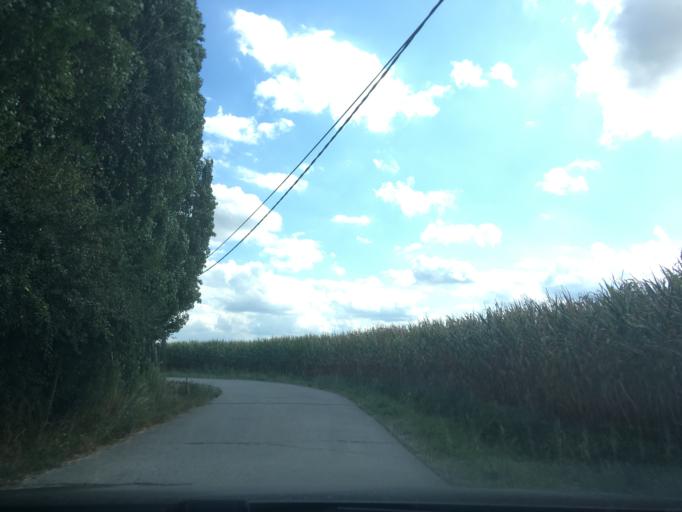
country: BE
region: Flanders
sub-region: Provincie West-Vlaanderen
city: Staden
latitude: 50.9800
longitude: 3.0396
